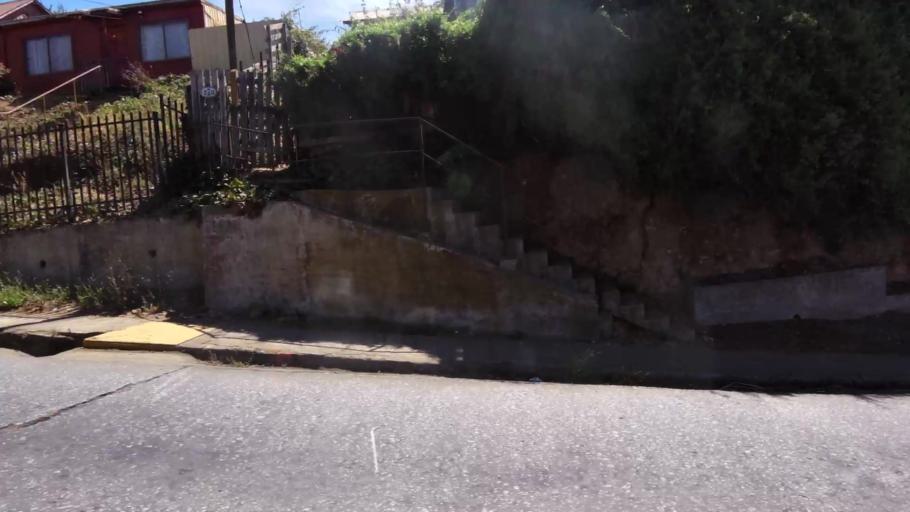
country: CL
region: Biobio
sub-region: Provincia de Concepcion
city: Talcahuano
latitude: -36.7164
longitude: -73.1219
